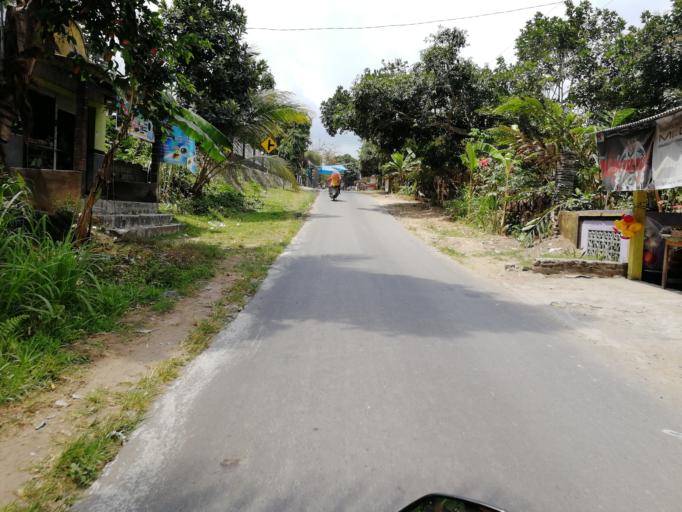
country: ID
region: West Nusa Tenggara
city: Pediti
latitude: -8.5623
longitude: 116.3317
